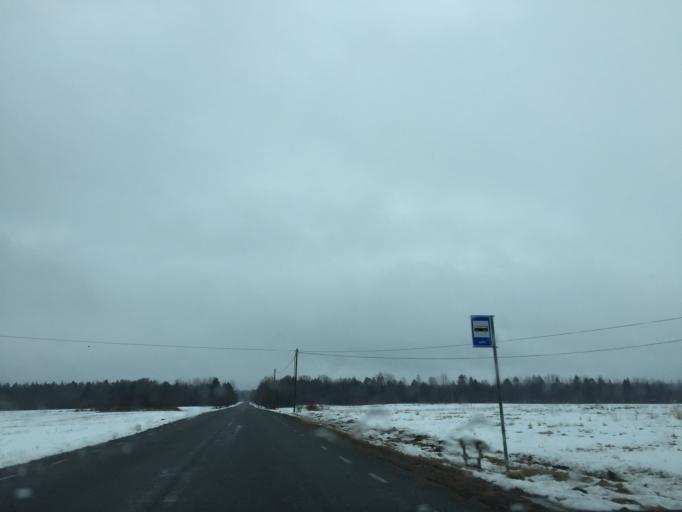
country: EE
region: Saare
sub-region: Kuressaare linn
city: Kuressaare
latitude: 58.3428
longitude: 22.0302
